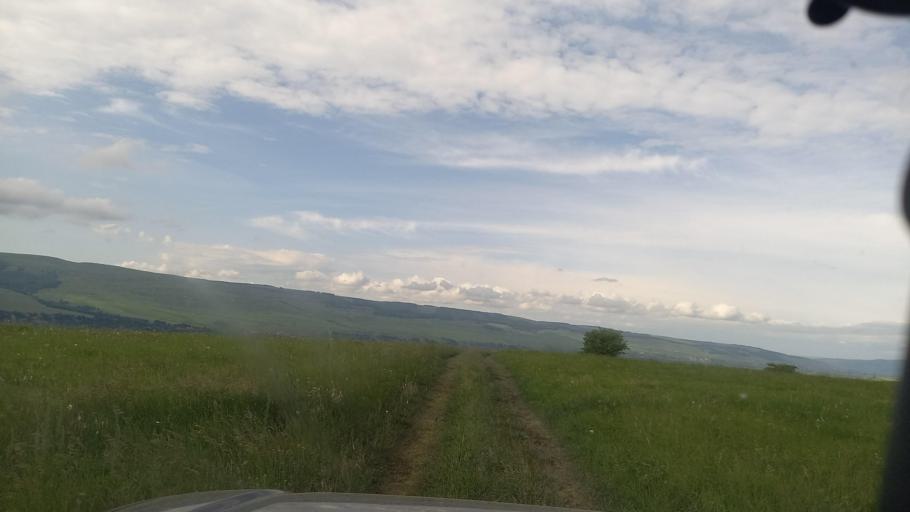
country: RU
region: Krasnodarskiy
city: Peredovaya
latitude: 44.0751
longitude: 41.3659
